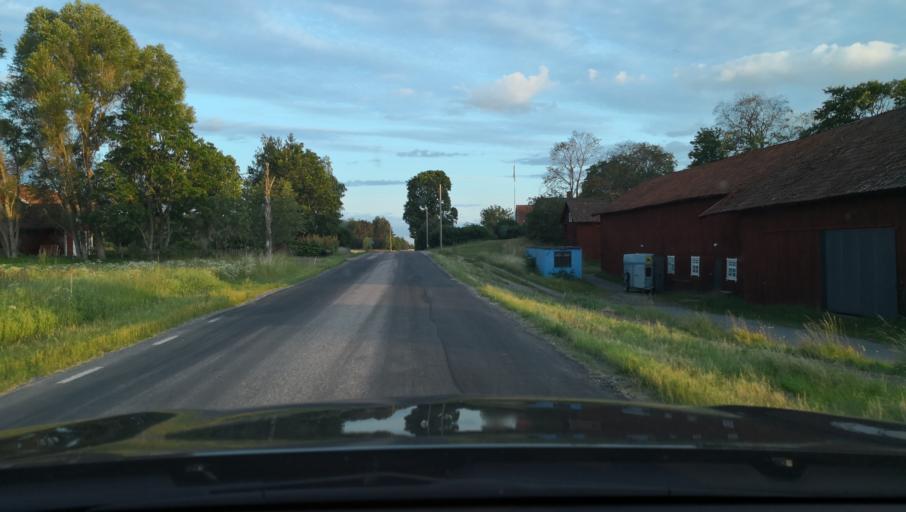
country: SE
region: Uppsala
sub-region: Uppsala Kommun
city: Vattholma
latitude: 60.0214
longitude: 17.7215
